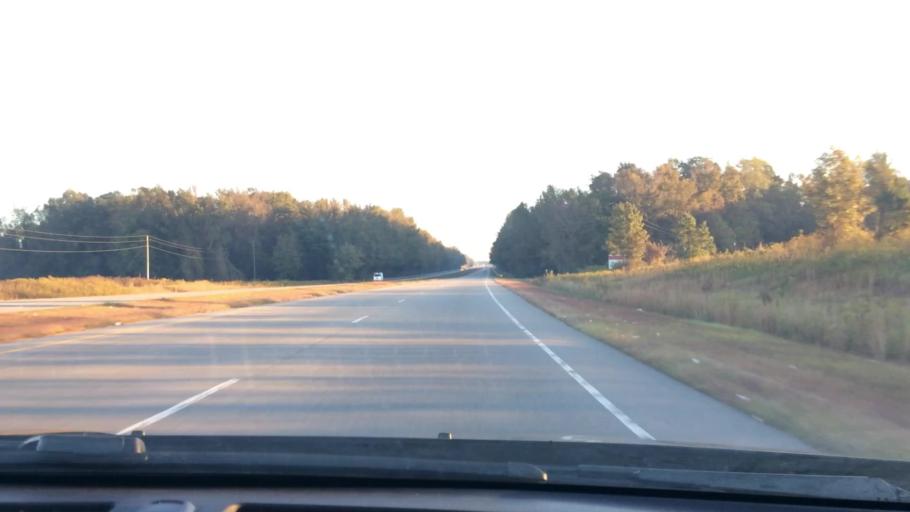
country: US
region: North Carolina
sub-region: Pitt County
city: Ayden
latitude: 35.4942
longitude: -77.4275
